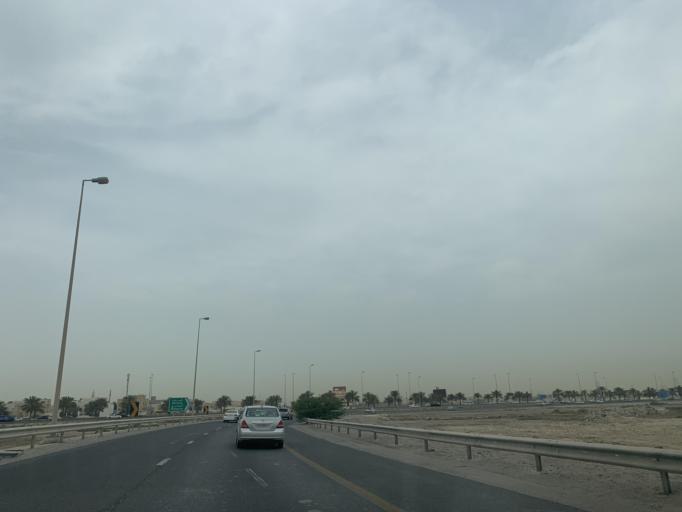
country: BH
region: Northern
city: Madinat `Isa
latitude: 26.1907
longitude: 50.5181
